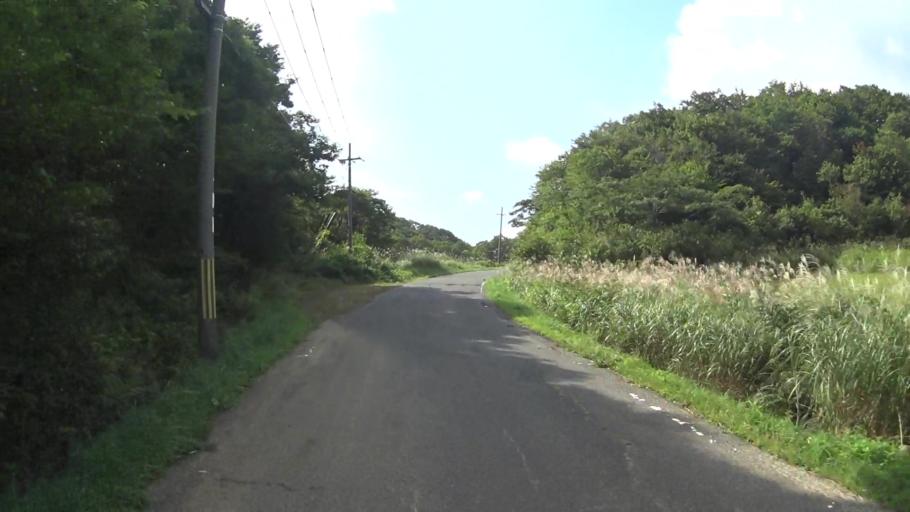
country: JP
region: Kyoto
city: Miyazu
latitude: 35.6524
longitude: 135.1810
